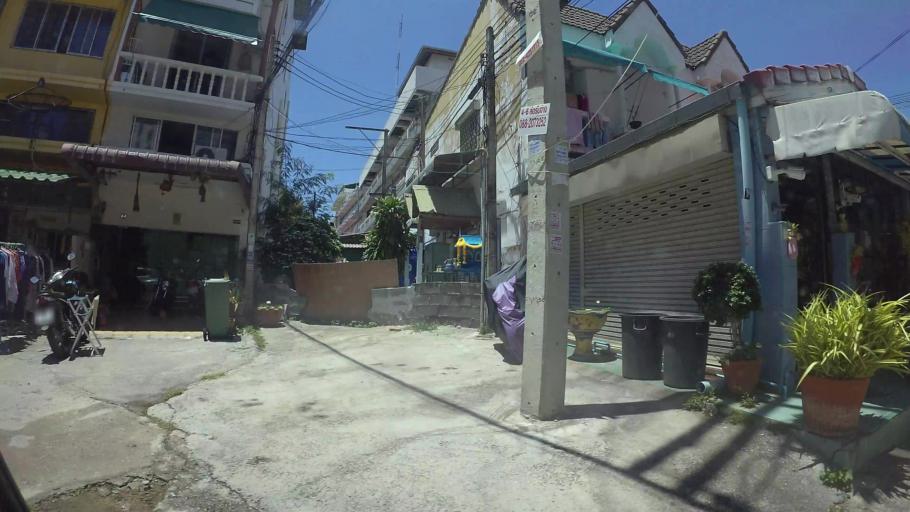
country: TH
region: Chon Buri
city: Phatthaya
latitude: 12.9317
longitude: 100.8931
